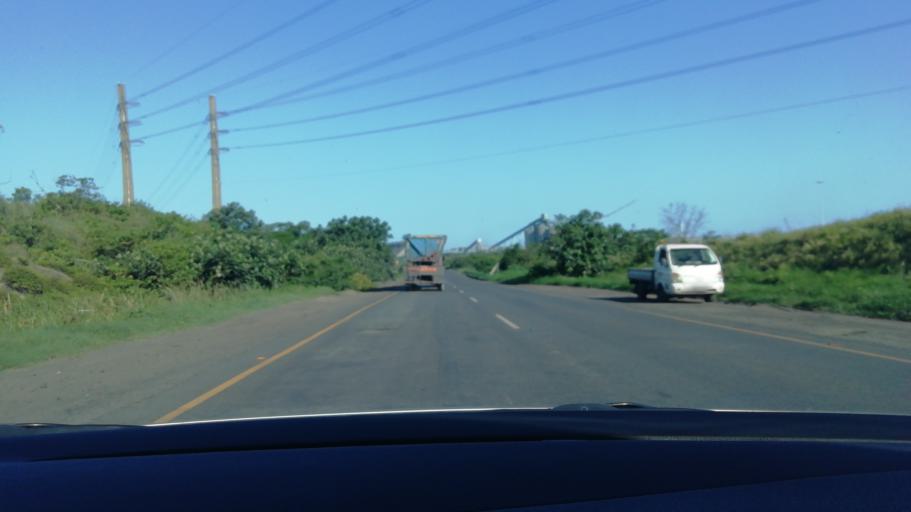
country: ZA
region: KwaZulu-Natal
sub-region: uThungulu District Municipality
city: Richards Bay
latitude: -28.7795
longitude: 32.0230
